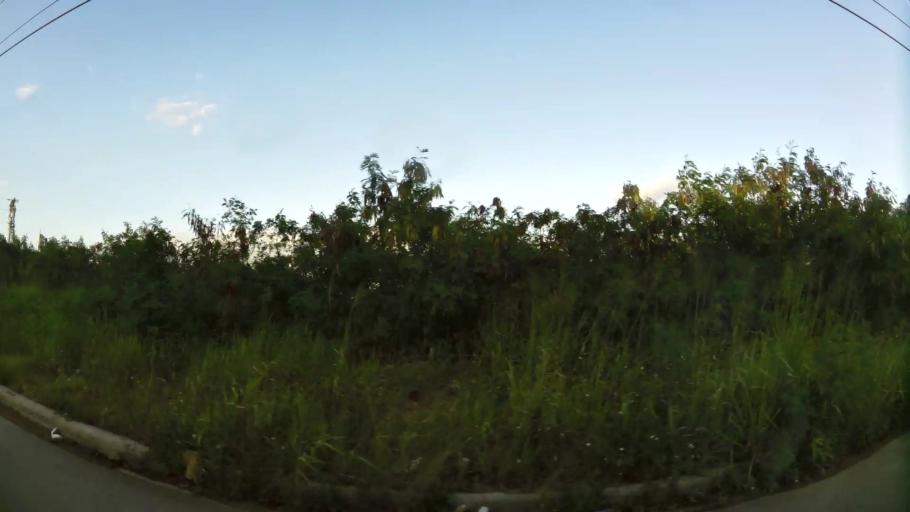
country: DO
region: Santo Domingo
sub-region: Santo Domingo
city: Santo Domingo Este
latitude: 18.4896
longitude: -69.8167
